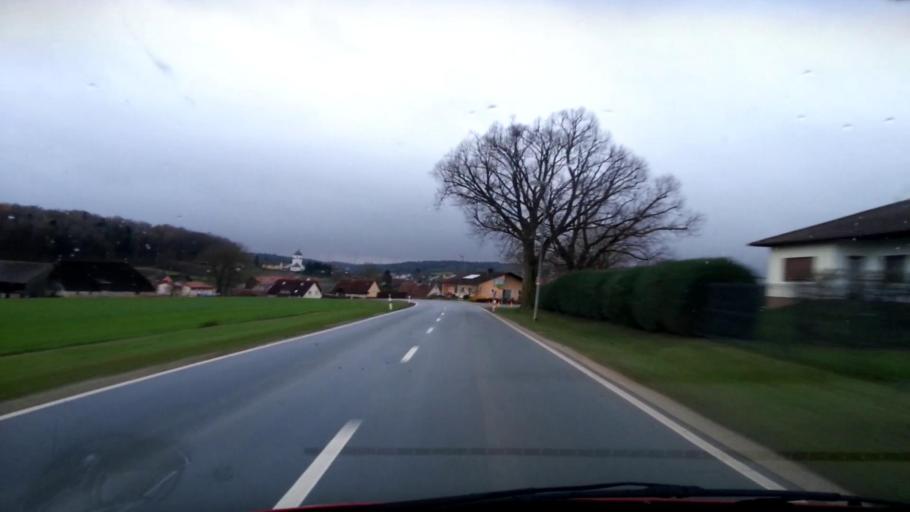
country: DE
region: Bavaria
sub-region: Upper Franconia
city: Konigsfeld
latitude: 49.9459
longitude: 11.1744
